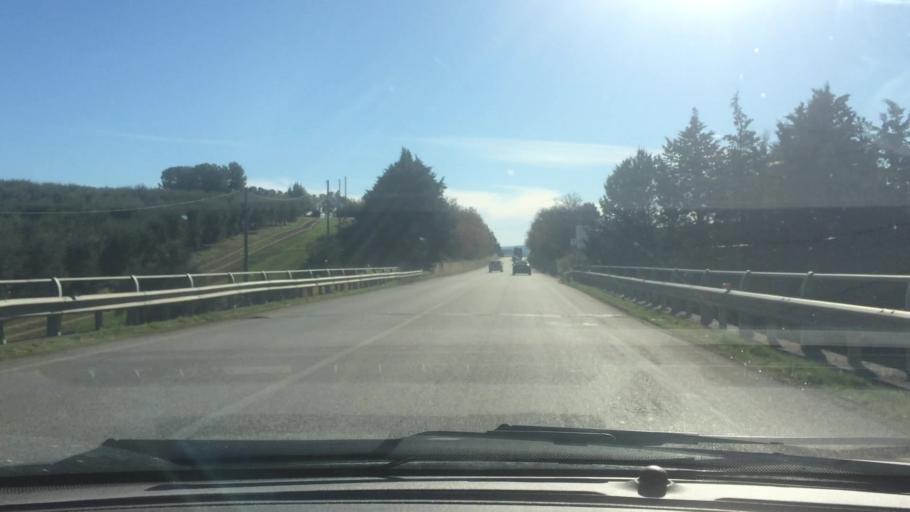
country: IT
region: Basilicate
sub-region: Provincia di Matera
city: Miglionico
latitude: 40.5910
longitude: 16.5740
